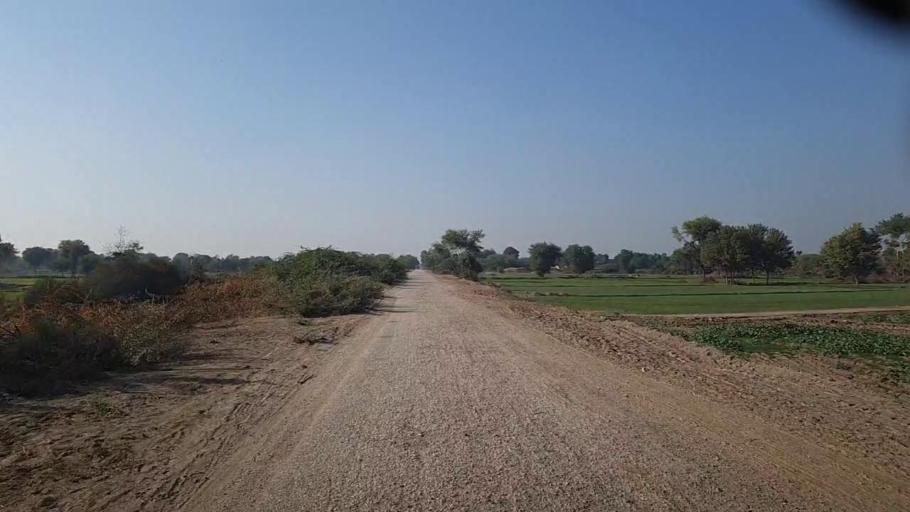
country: PK
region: Sindh
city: Darya Khan Marri
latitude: 26.6724
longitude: 68.3830
